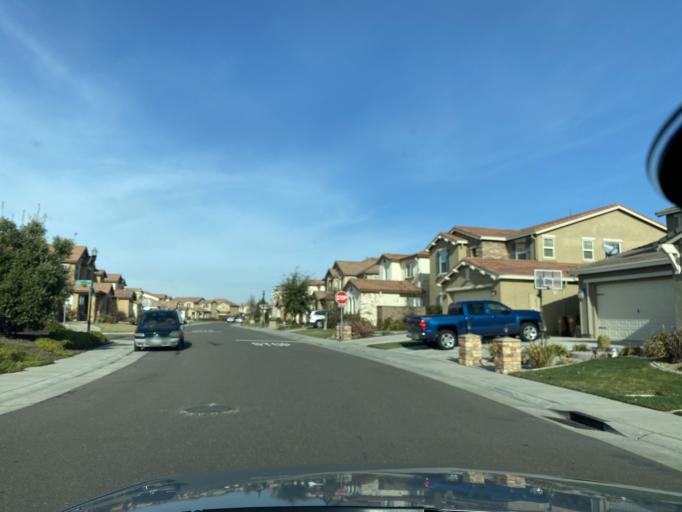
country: US
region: California
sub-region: Sacramento County
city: Elk Grove
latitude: 38.4039
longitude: -121.3966
